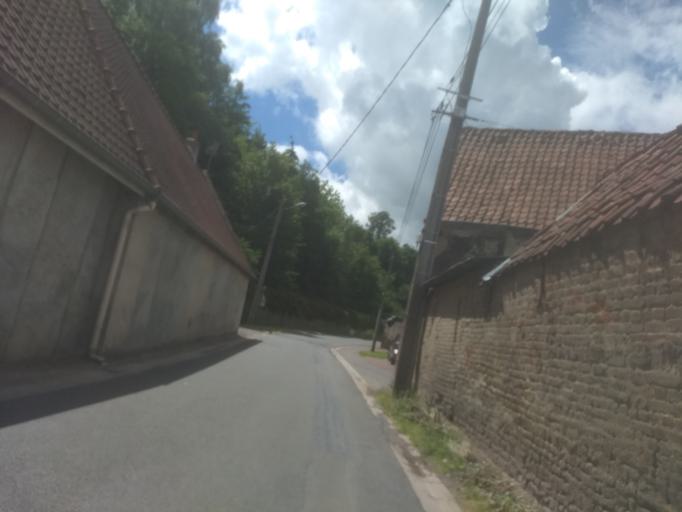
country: FR
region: Nord-Pas-de-Calais
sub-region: Departement du Pas-de-Calais
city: Riviere
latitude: 50.2382
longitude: 2.6992
